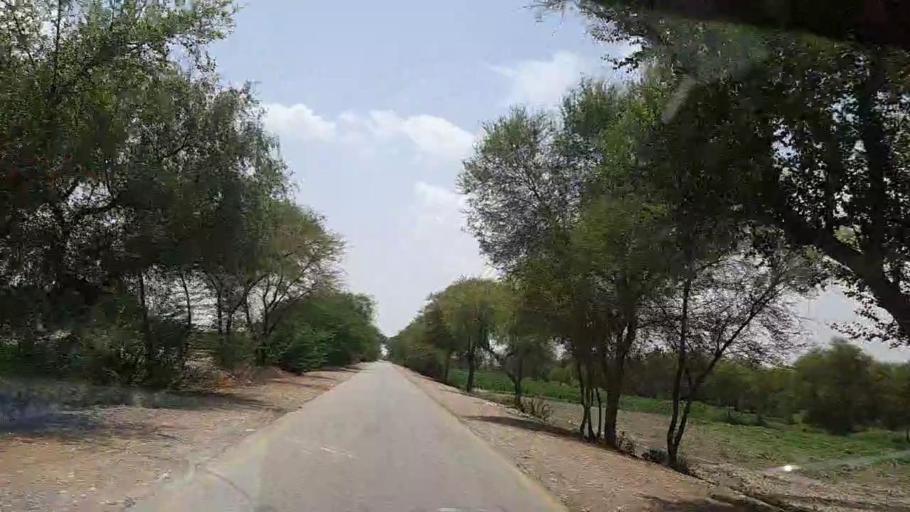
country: PK
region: Sindh
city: Bhan
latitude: 26.5415
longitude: 67.6948
